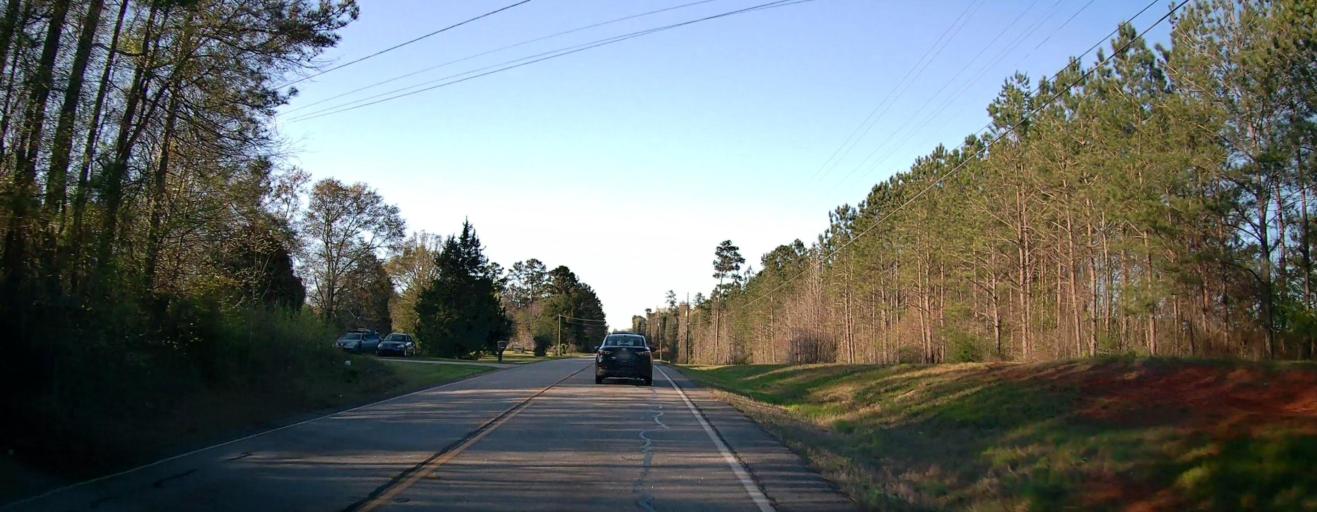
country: US
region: Georgia
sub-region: Butts County
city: Jackson
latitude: 33.4219
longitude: -83.8951
